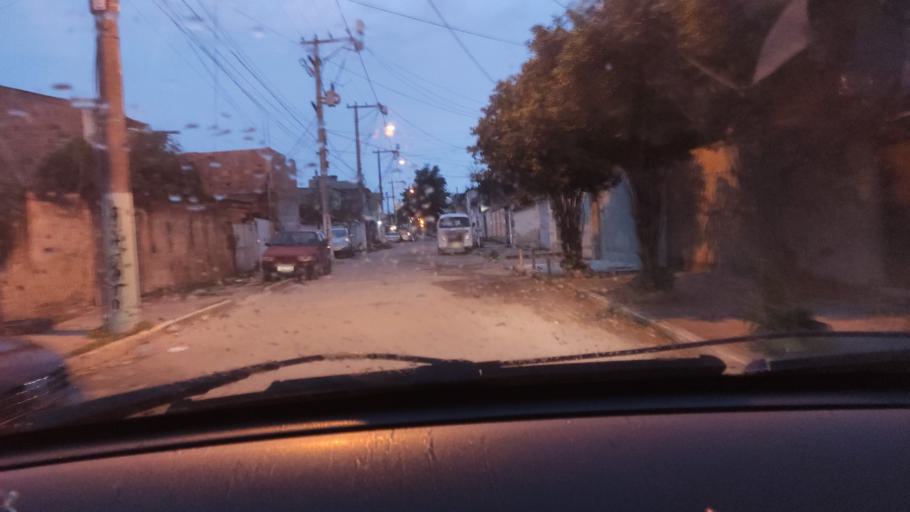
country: BR
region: Rio de Janeiro
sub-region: Itaborai
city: Itaborai
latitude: -22.7782
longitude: -42.9405
